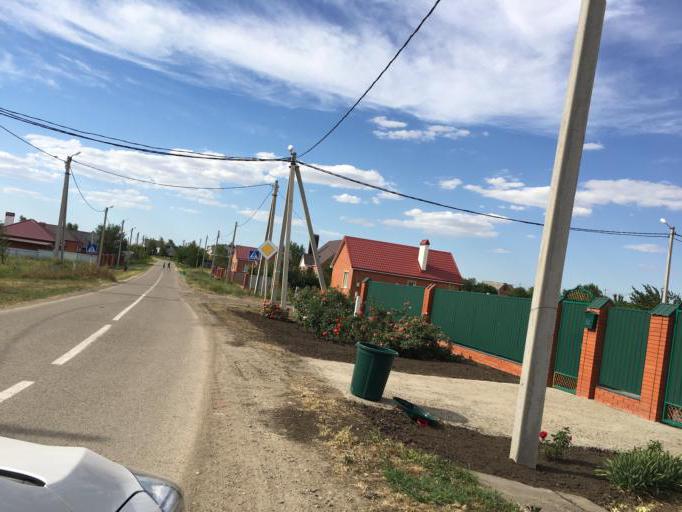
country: RU
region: Krasnodarskiy
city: Kushchevskaya
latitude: 46.5533
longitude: 39.6743
